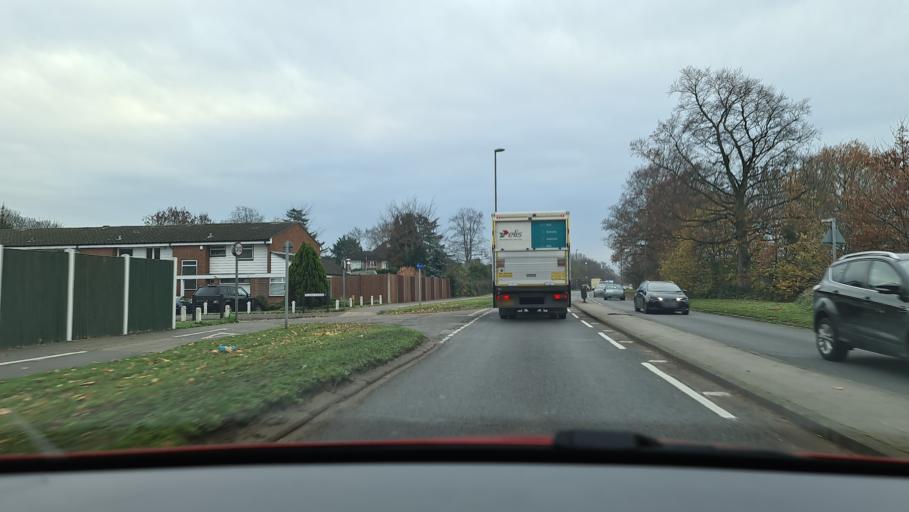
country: GB
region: England
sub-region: Surrey
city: East Molesey
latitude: 51.3967
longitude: -0.3425
